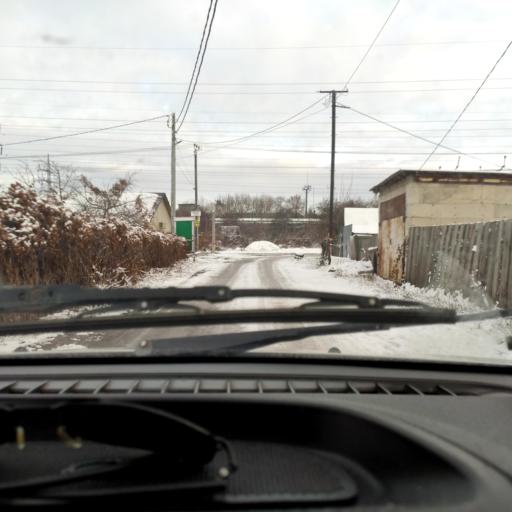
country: RU
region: Samara
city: Tol'yatti
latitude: 53.5418
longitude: 49.4397
